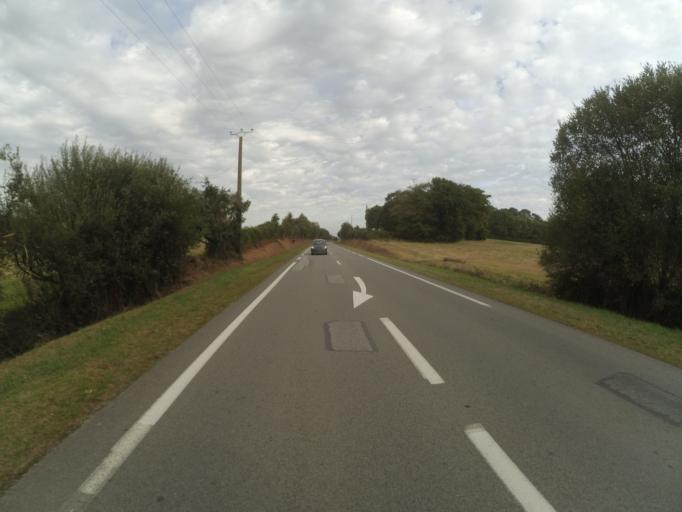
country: FR
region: Brittany
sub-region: Departement du Morbihan
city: Merlevenez
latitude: 47.7274
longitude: -3.2300
